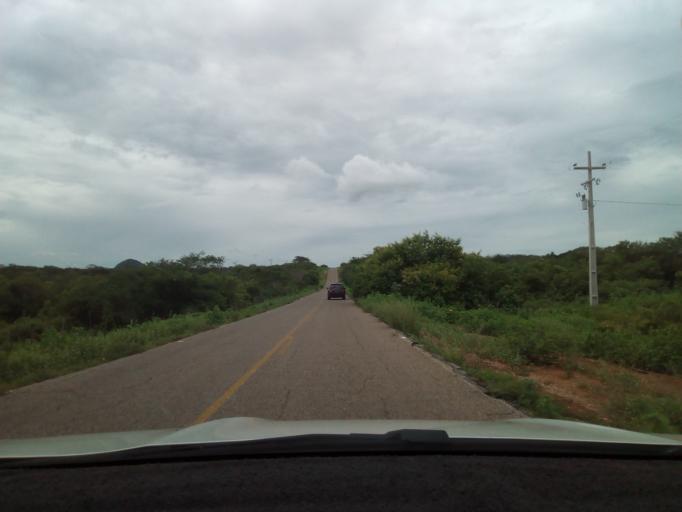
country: BR
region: Rio Grande do Norte
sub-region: Patu
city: Patu
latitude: -6.1192
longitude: -37.7374
